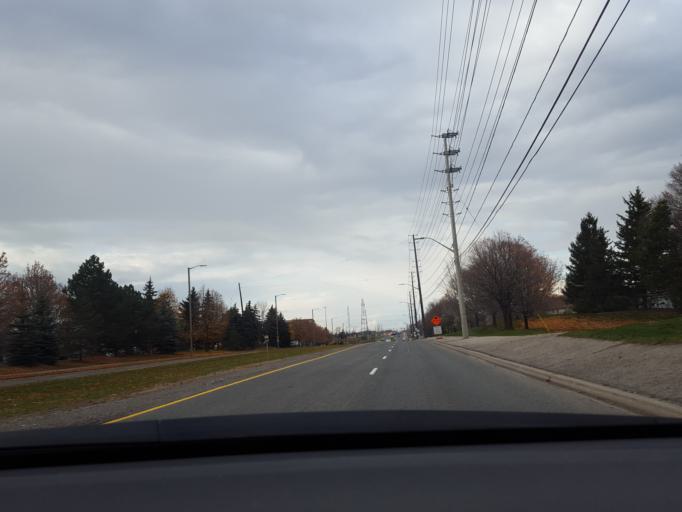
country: CA
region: Ontario
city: Mississauga
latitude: 43.5374
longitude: -79.7015
